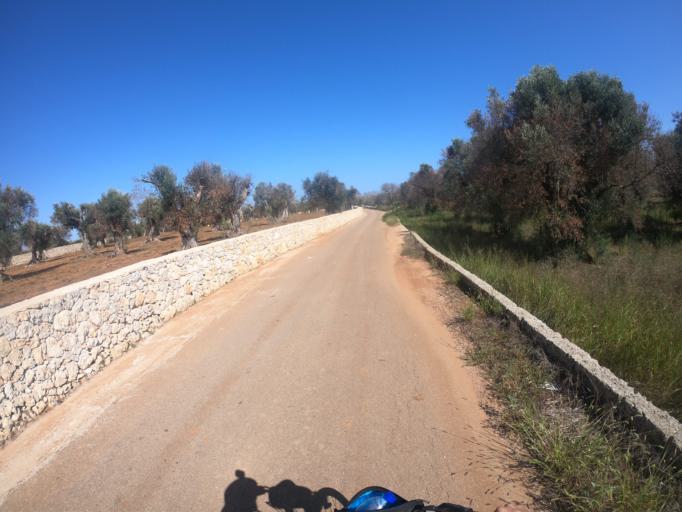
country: IT
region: Apulia
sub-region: Provincia di Lecce
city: Presicce
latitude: 39.9198
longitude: 18.2775
